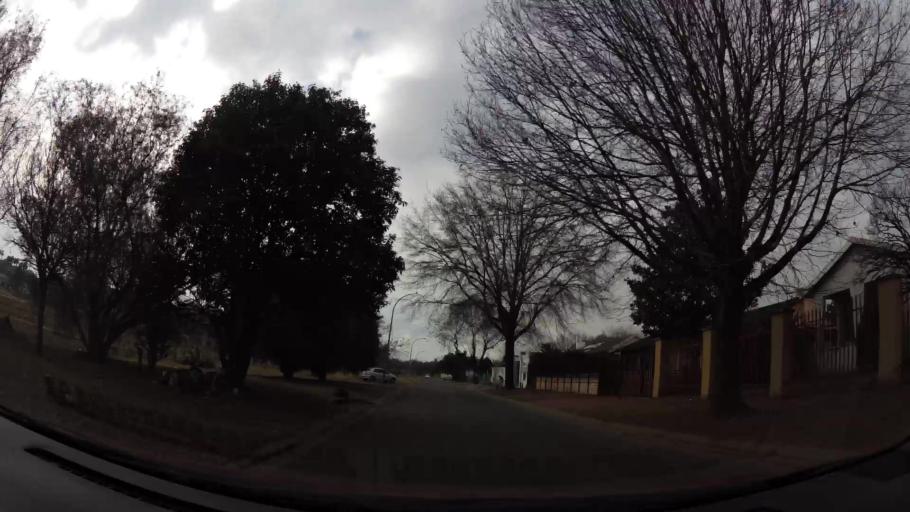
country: ZA
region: Gauteng
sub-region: Sedibeng District Municipality
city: Vanderbijlpark
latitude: -26.7138
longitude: 27.8600
